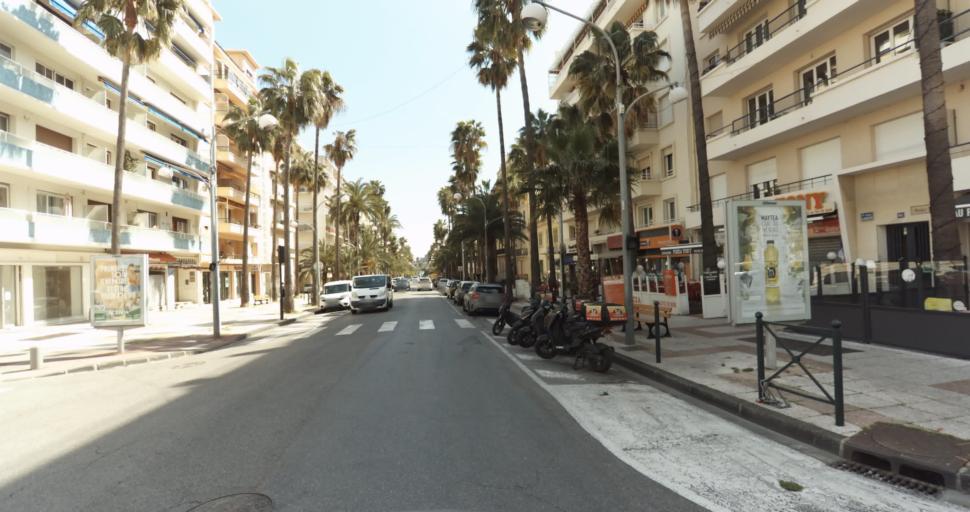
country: FR
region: Provence-Alpes-Cote d'Azur
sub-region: Departement du Var
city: Hyeres
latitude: 43.1171
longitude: 6.1286
